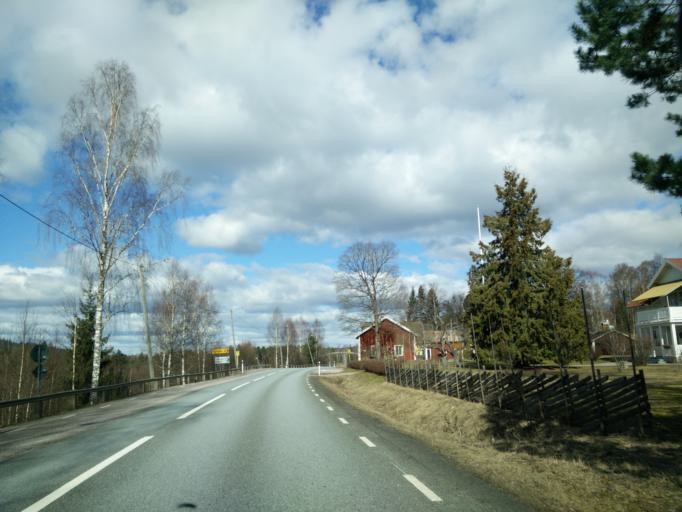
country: SE
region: Vaermland
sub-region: Munkfors Kommun
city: Munkfors
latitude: 59.9021
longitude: 13.5588
